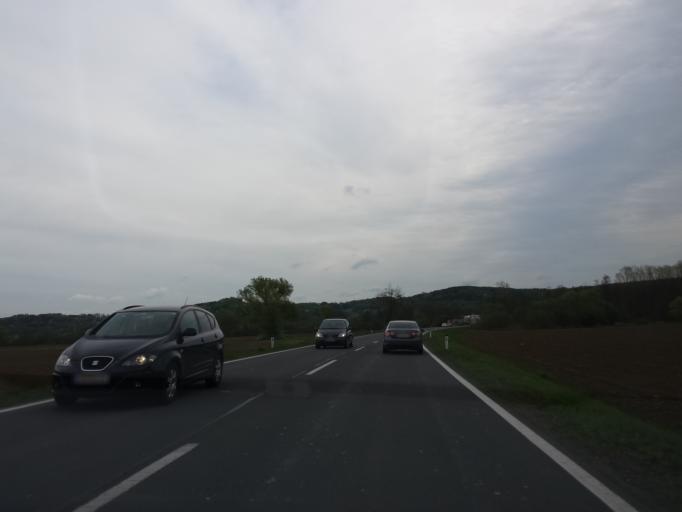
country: AT
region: Styria
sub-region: Politischer Bezirk Hartberg-Fuerstenfeld
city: Fuerstenfeld
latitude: 47.0532
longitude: 16.0997
